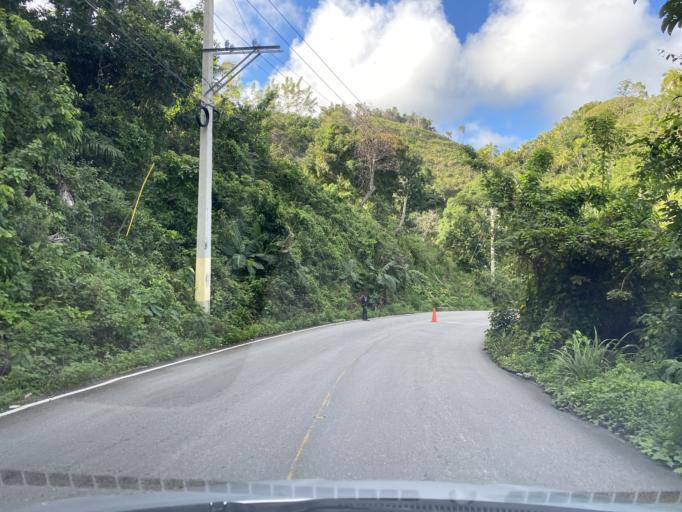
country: DO
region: Samana
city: Las Terrenas
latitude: 19.2665
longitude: -69.5657
